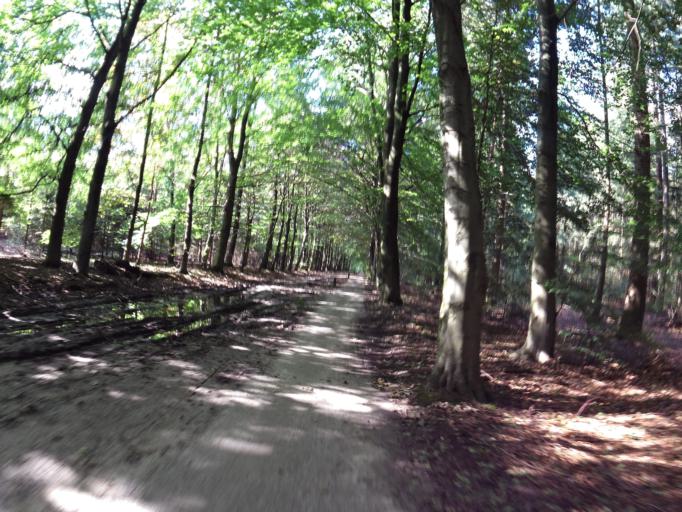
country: NL
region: North Brabant
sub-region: Gemeente Heeze-Leende
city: Heeze
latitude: 51.3909
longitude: 5.5527
